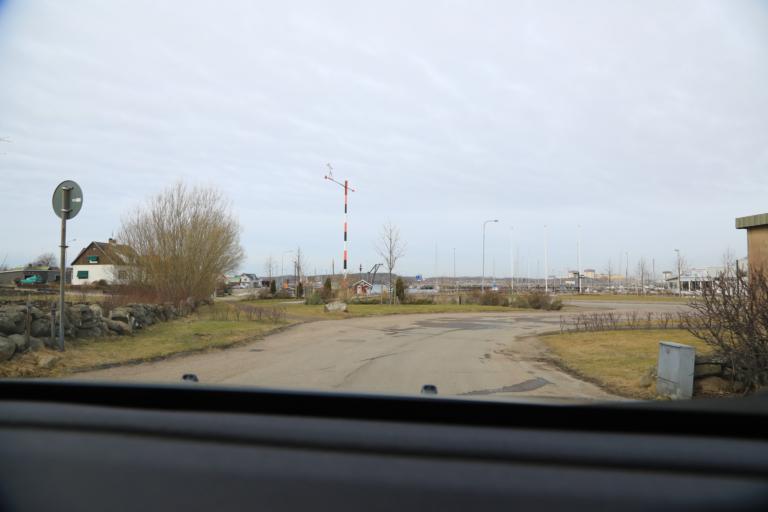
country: SE
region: Halland
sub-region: Kungsbacka Kommun
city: Frillesas
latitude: 57.2385
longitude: 12.1153
